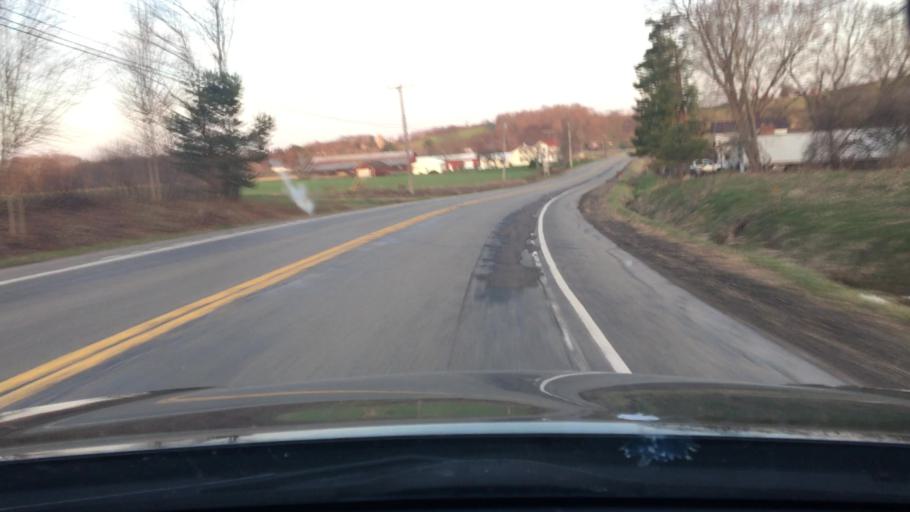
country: US
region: New York
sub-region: Cattaraugus County
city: Randolph
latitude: 42.1947
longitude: -78.9030
